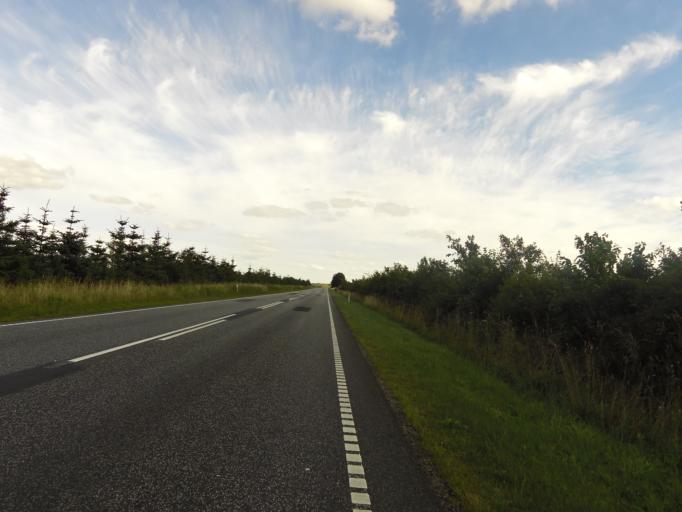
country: DK
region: South Denmark
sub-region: Tonder Kommune
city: Toftlund
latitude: 55.2104
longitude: 9.0428
